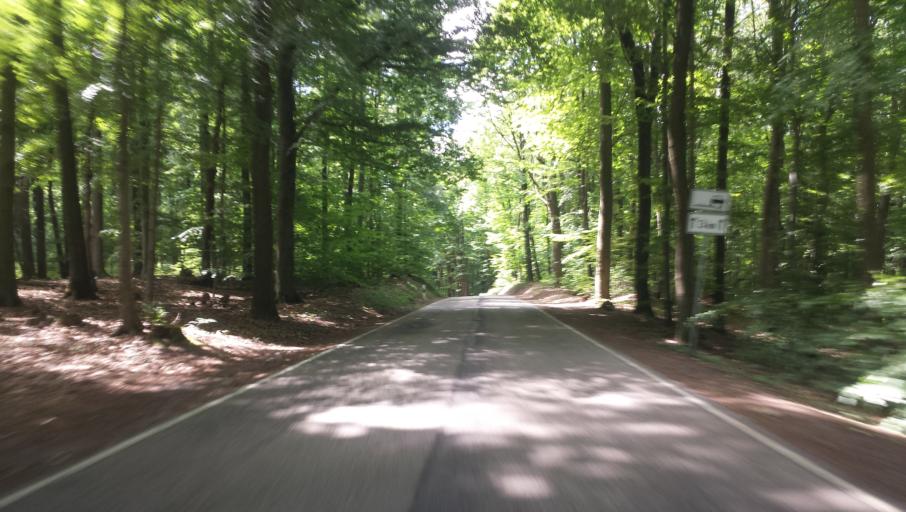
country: DE
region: Rheinland-Pfalz
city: Waldhambach
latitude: 49.1862
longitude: 7.9832
